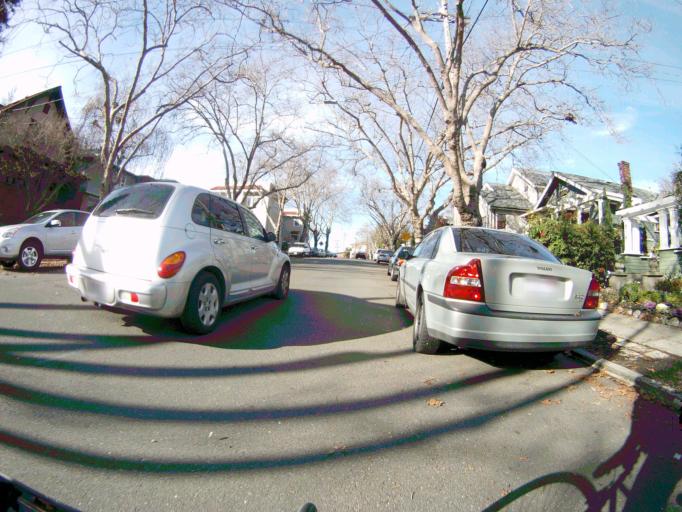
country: US
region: California
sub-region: Alameda County
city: Piedmont
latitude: 37.8244
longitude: -122.2473
